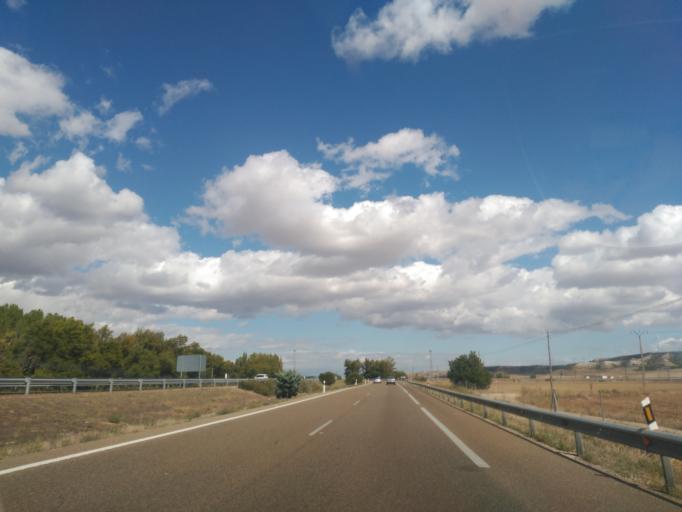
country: ES
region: Castille and Leon
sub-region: Provincia de Palencia
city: Cordovilla la Real
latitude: 42.0406
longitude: -4.2674
